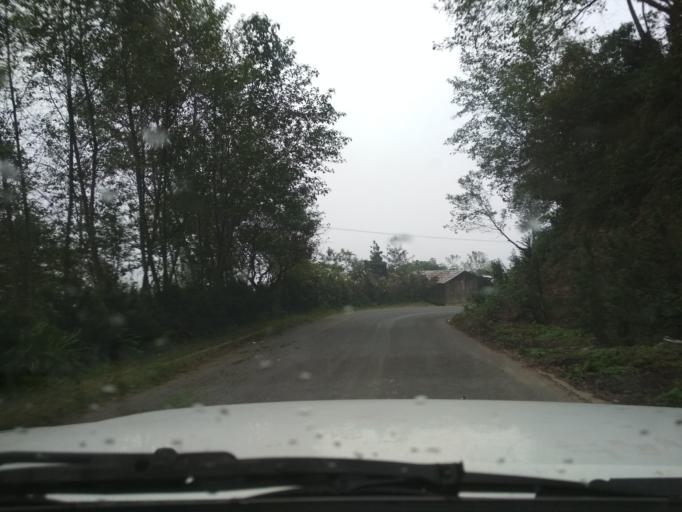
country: MX
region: Veracruz
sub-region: La Perla
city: Metlac Hernandez (Metlac Primero)
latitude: 18.9520
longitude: -97.1674
